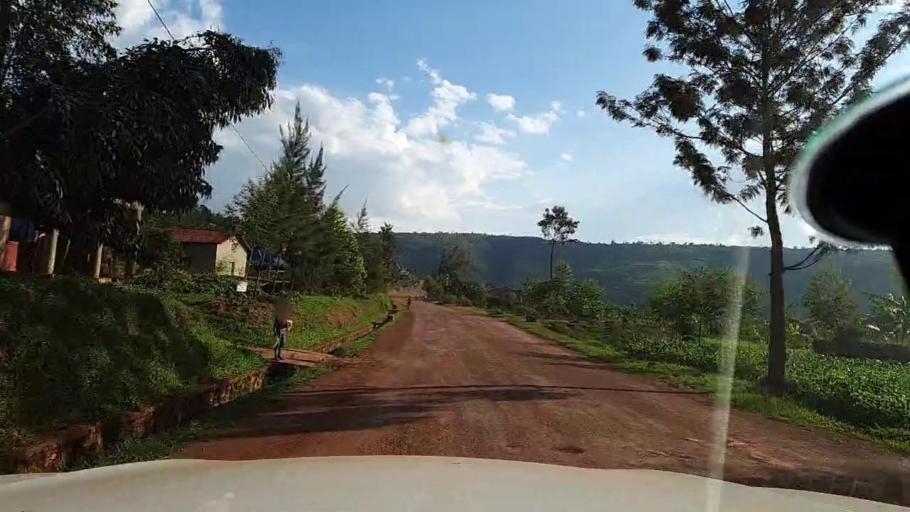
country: RW
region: Kigali
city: Kigali
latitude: -1.8970
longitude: 29.9648
